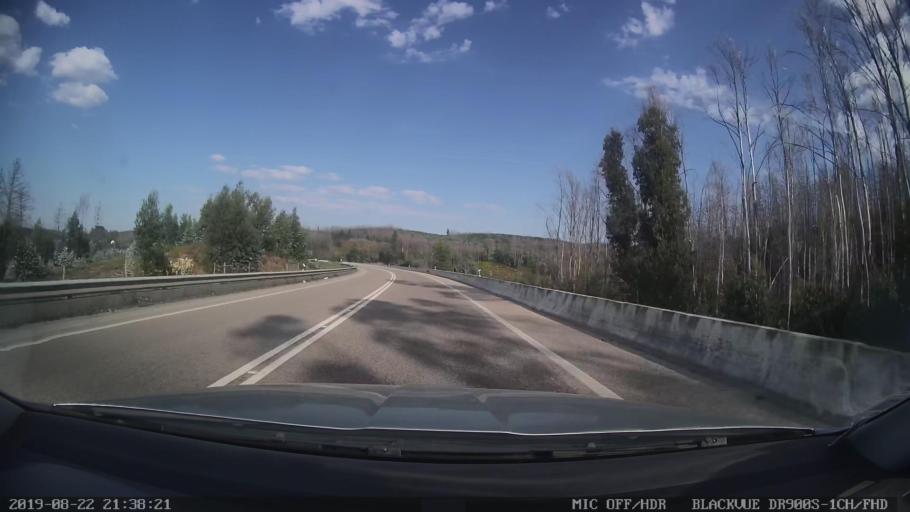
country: PT
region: Leiria
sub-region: Figueiro Dos Vinhos
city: Figueiro dos Vinhos
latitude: 39.9357
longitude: -8.2663
